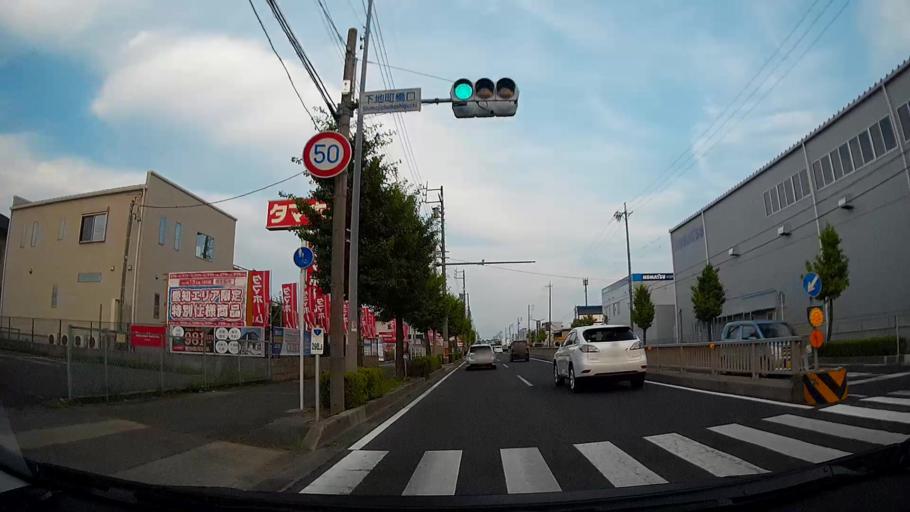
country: JP
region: Aichi
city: Toyohashi
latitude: 34.7835
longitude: 137.3802
